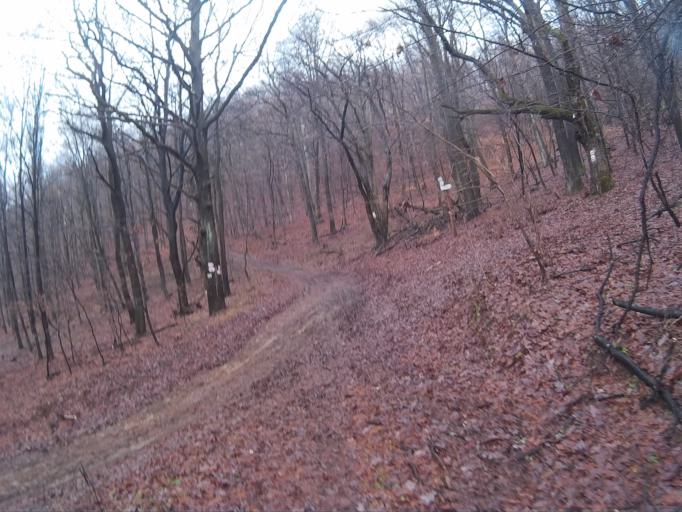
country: HU
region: Nograd
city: Somoskoujfalu
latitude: 48.1546
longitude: 19.7919
